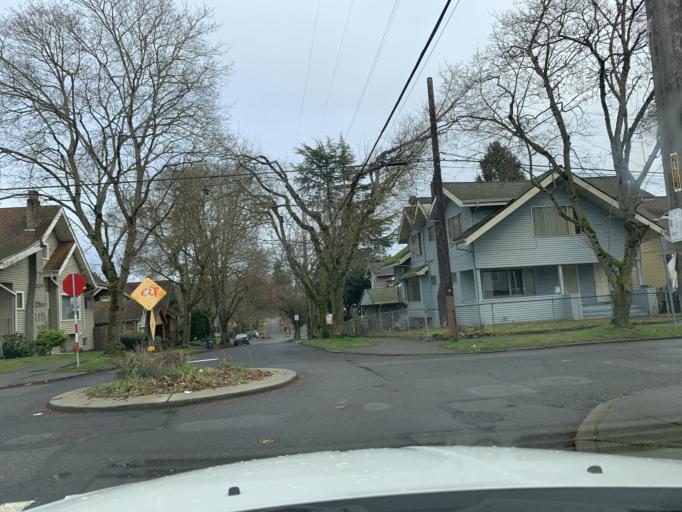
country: US
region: Washington
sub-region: King County
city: Seattle
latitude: 47.6043
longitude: -122.3001
